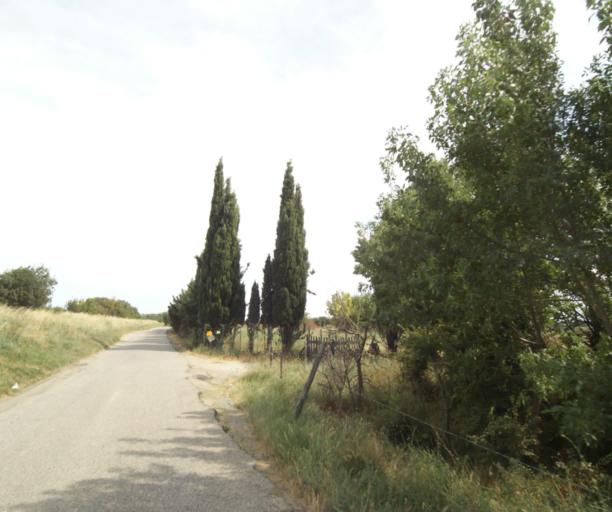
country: FR
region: Languedoc-Roussillon
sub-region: Departement de l'Herault
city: Marsillargues
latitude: 43.6859
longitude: 4.1638
